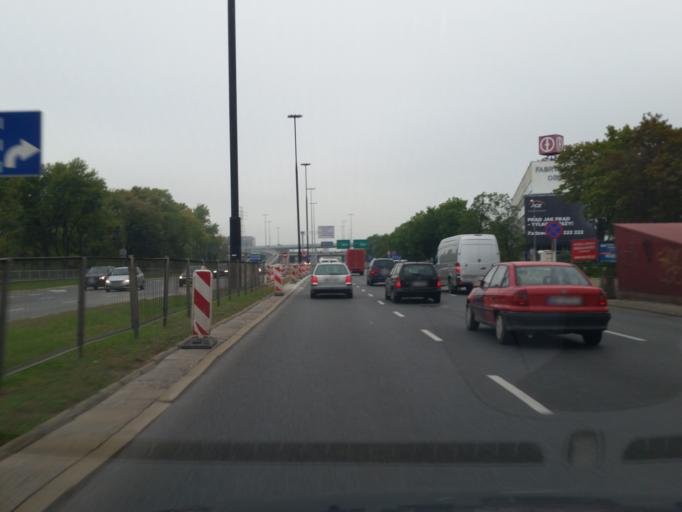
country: PL
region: Masovian Voivodeship
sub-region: Warszawa
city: Zoliborz
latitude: 52.2870
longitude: 21.0065
